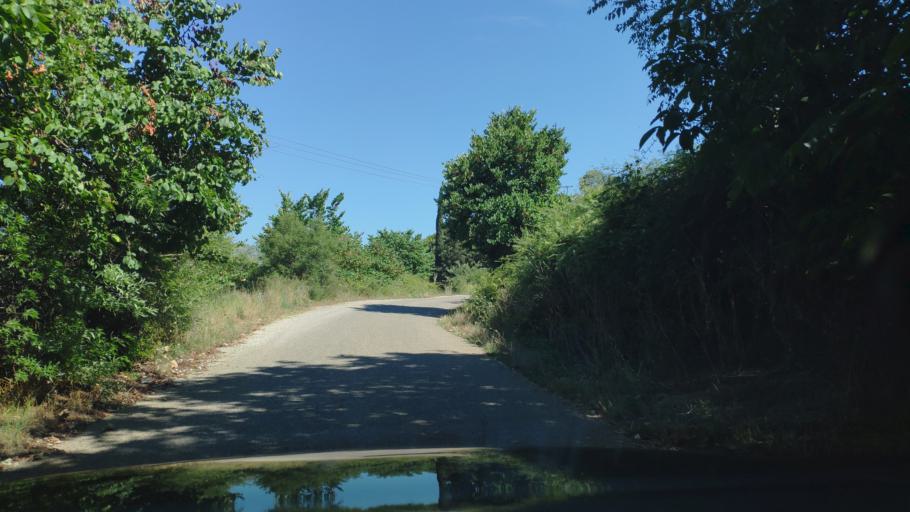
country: GR
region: West Greece
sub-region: Nomos Aitolias kai Akarnanias
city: Katouna
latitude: 38.8367
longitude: 21.0972
